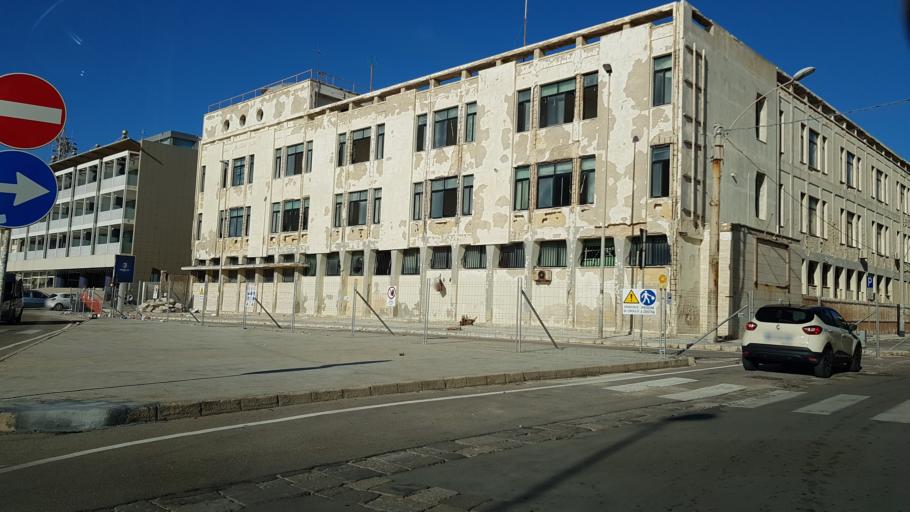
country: IT
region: Apulia
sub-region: Provincia di Lecce
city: Gallipoli
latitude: 40.0548
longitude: 17.9846
